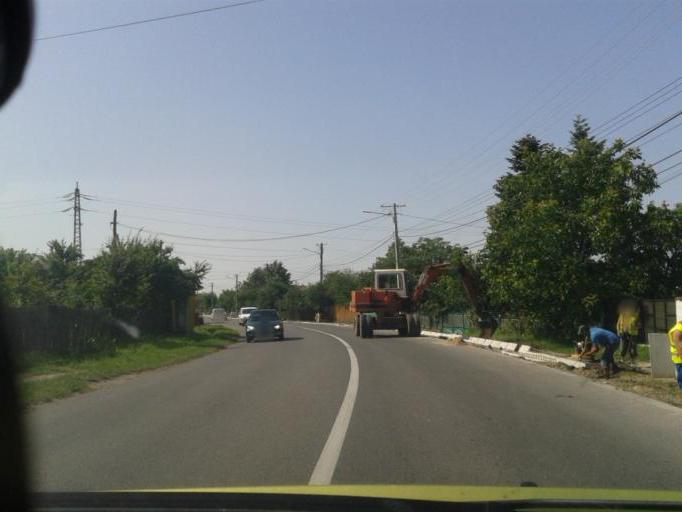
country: RO
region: Prahova
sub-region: Comuna Paulesti
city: Gageni
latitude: 45.0257
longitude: 25.9431
